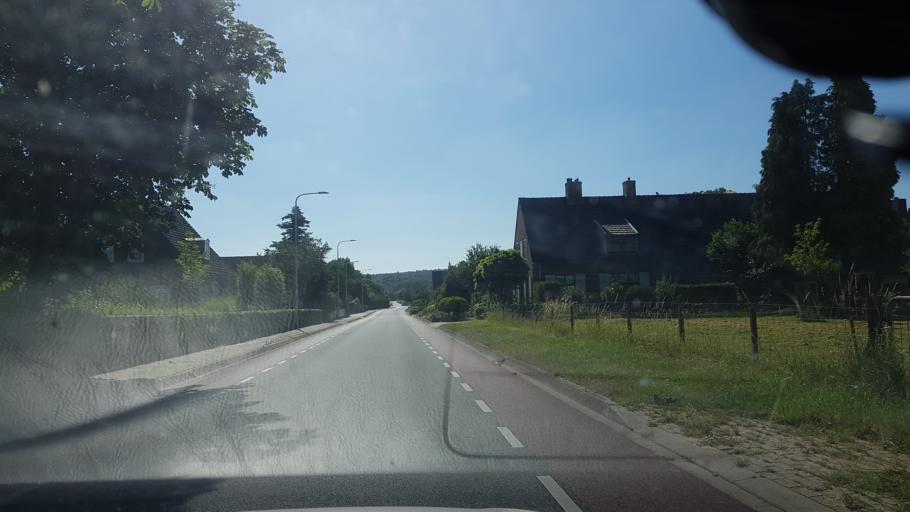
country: NL
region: Gelderland
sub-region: Gemeente Groesbeek
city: Bredeweg
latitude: 51.7520
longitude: 5.9427
